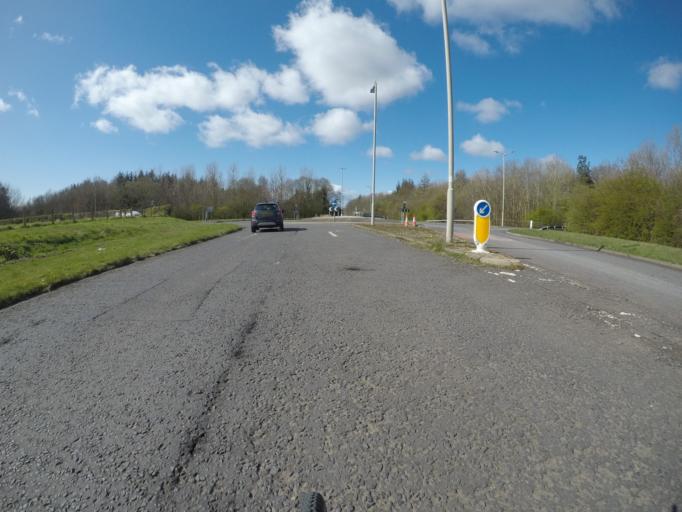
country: GB
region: Scotland
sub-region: North Ayrshire
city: Springside
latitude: 55.6125
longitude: -4.6033
